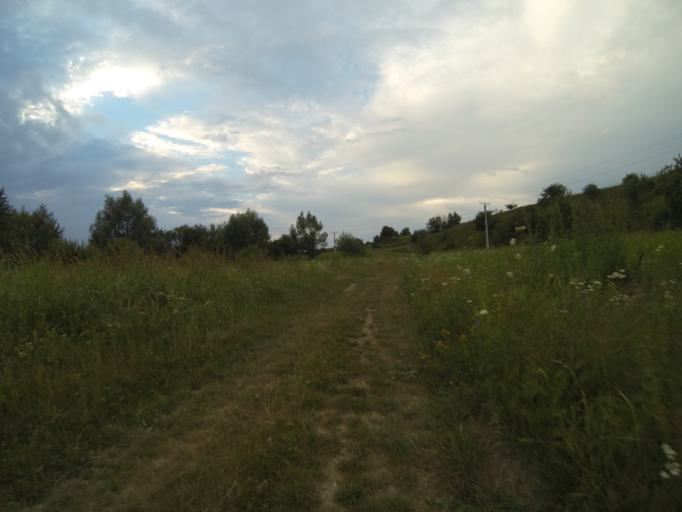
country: RO
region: Brasov
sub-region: Comuna Sinca Veche
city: Sinca Veche
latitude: 45.7751
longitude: 25.1629
